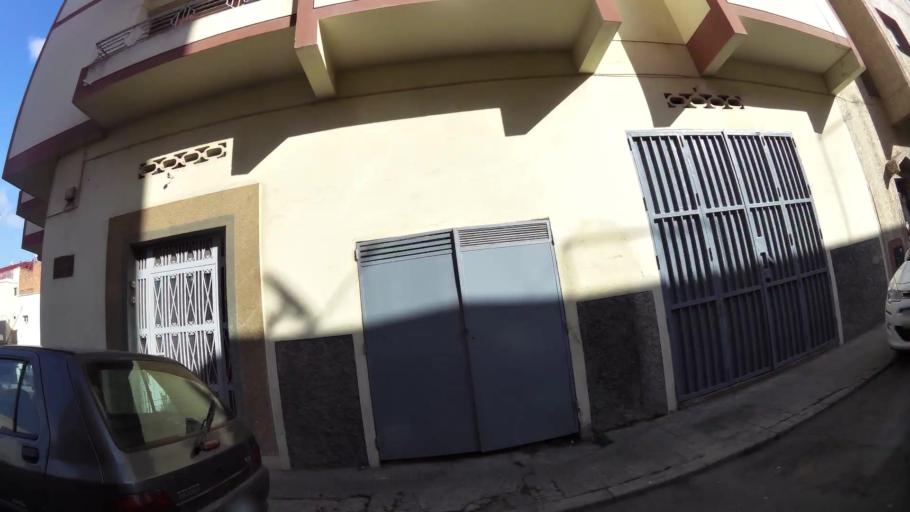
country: MA
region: Rabat-Sale-Zemmour-Zaer
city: Sale
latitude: 34.0461
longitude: -6.8086
